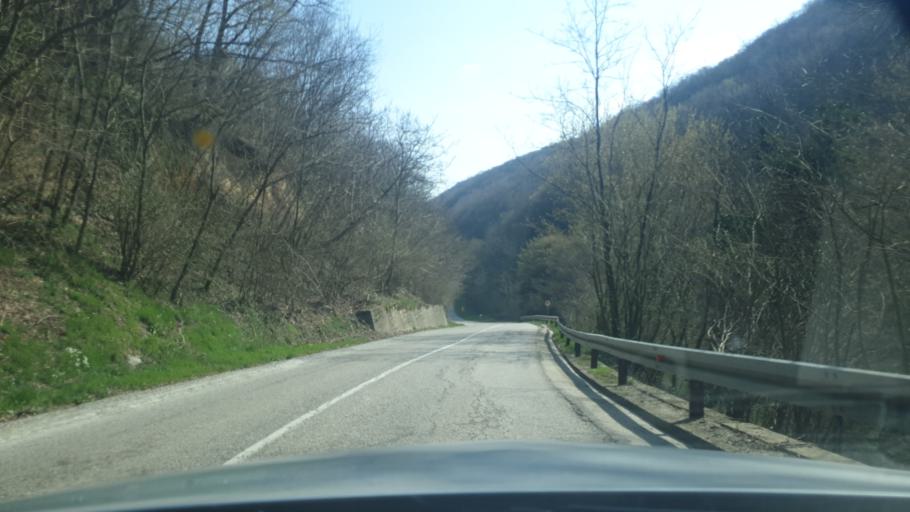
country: RS
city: Vrdnik
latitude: 45.1442
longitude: 19.7712
